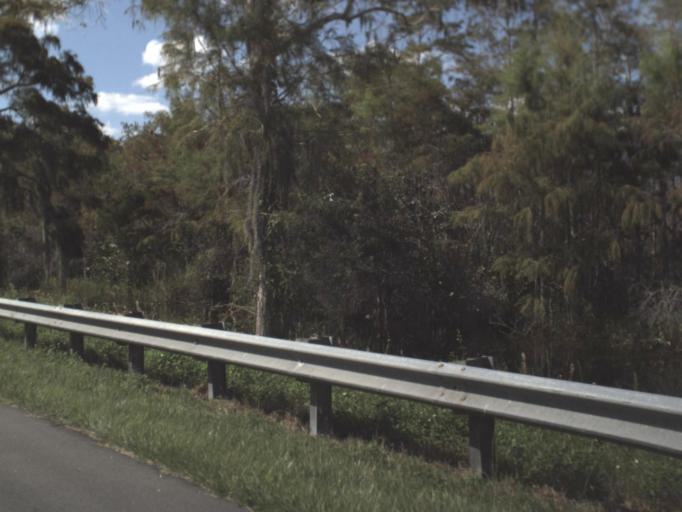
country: US
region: Florida
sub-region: Miami-Dade County
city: Kendall West
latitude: 25.8480
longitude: -80.9454
